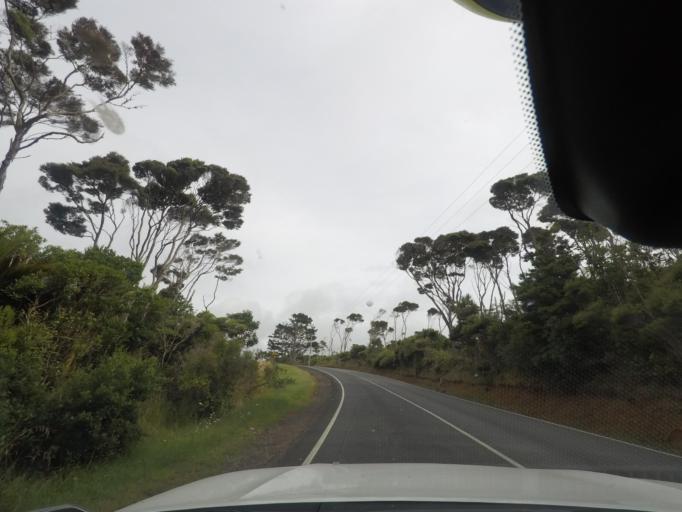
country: NZ
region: Auckland
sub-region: Auckland
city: Parakai
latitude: -36.4881
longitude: 174.2475
